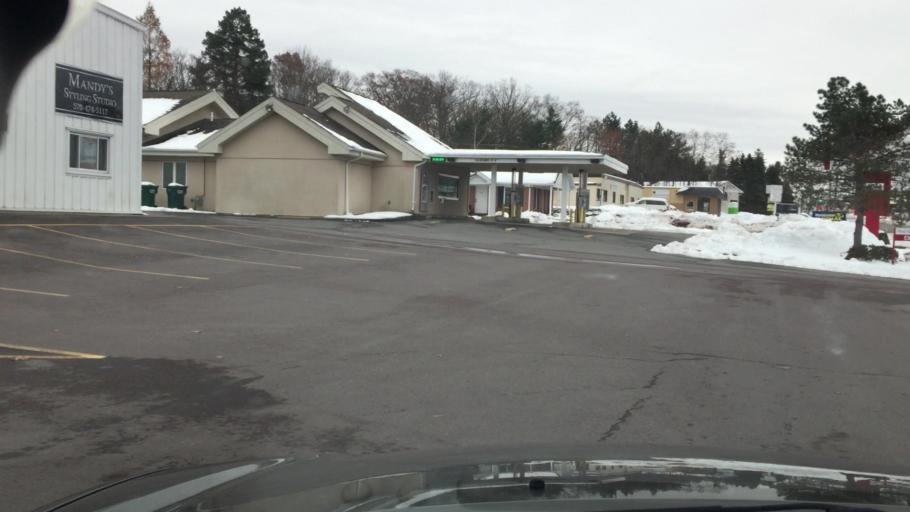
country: US
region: Pennsylvania
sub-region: Luzerne County
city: Mountain Top
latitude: 41.1599
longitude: -75.8875
